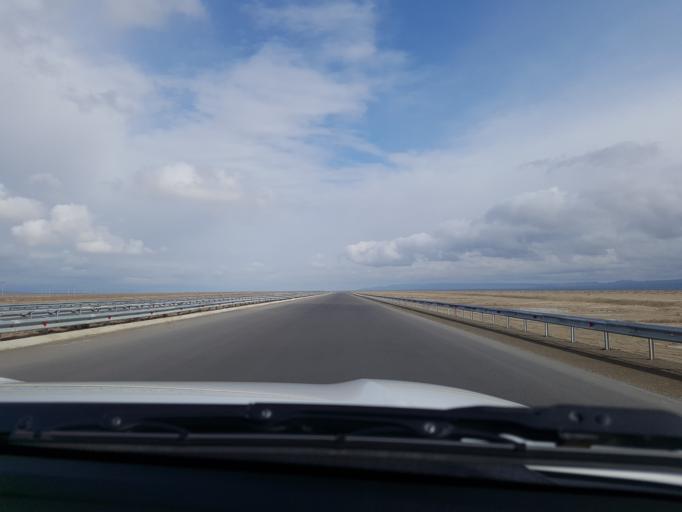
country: TM
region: Balkan
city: Gumdag
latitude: 39.1779
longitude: 54.9477
